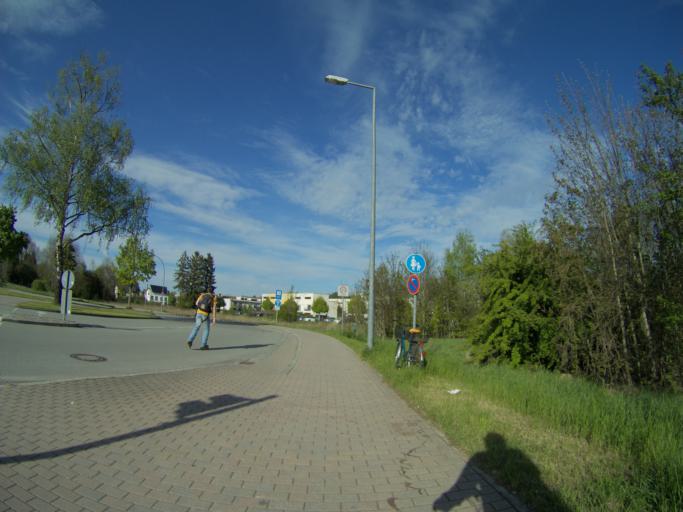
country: DE
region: Bavaria
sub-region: Upper Bavaria
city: Freising
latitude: 48.3870
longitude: 11.7374
